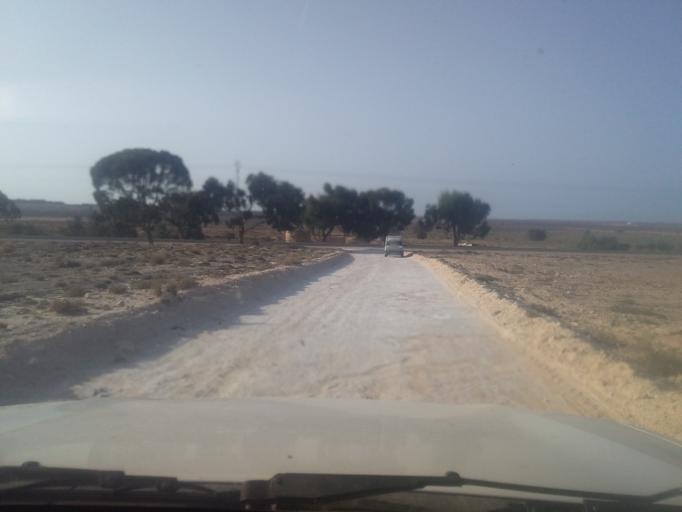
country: TN
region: Qabis
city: Gabes
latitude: 33.6404
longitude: 10.2922
